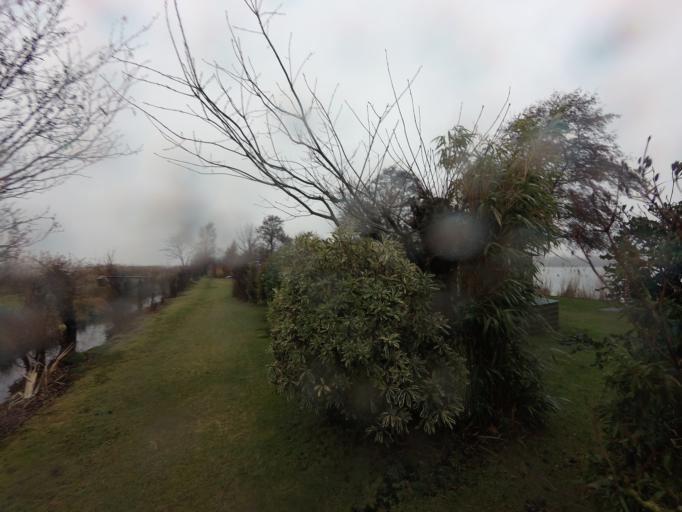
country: NL
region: South Holland
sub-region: Gemeente Vlist
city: Haastrecht
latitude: 52.0215
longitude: 4.7549
